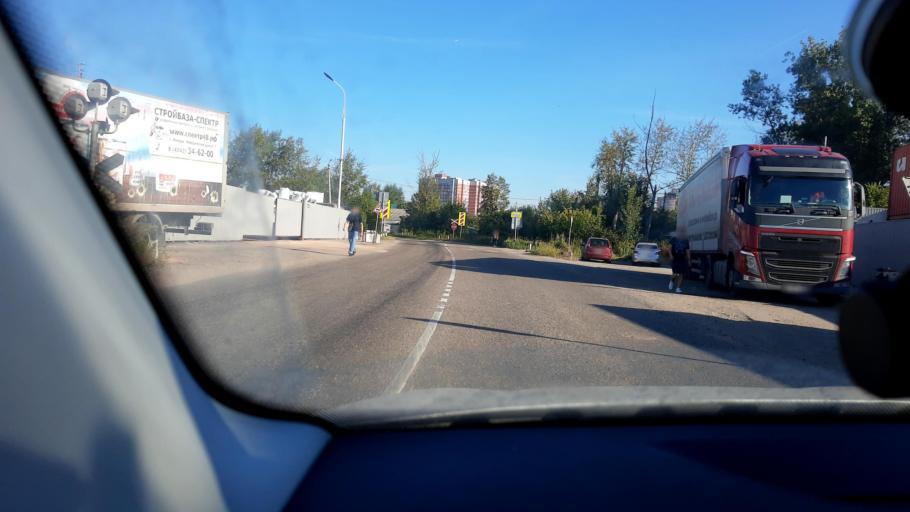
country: RU
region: Moskovskaya
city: Shcherbinka
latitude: 55.4660
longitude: 37.5687
